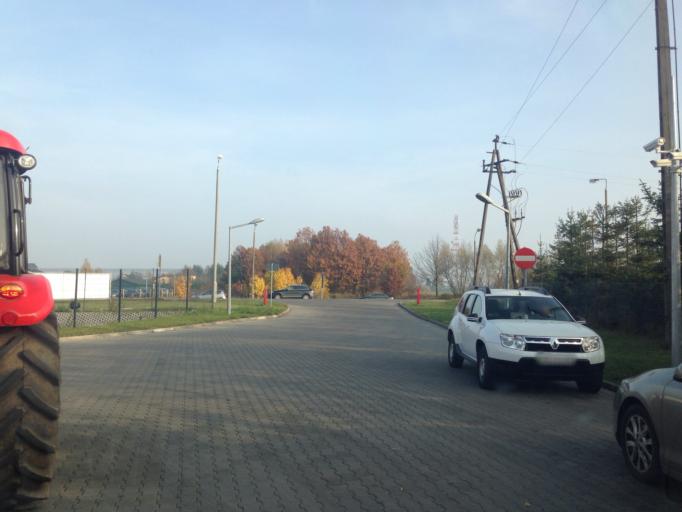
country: PL
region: Kujawsko-Pomorskie
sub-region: Powiat bydgoski
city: Osielsko
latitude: 53.1714
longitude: 18.0519
